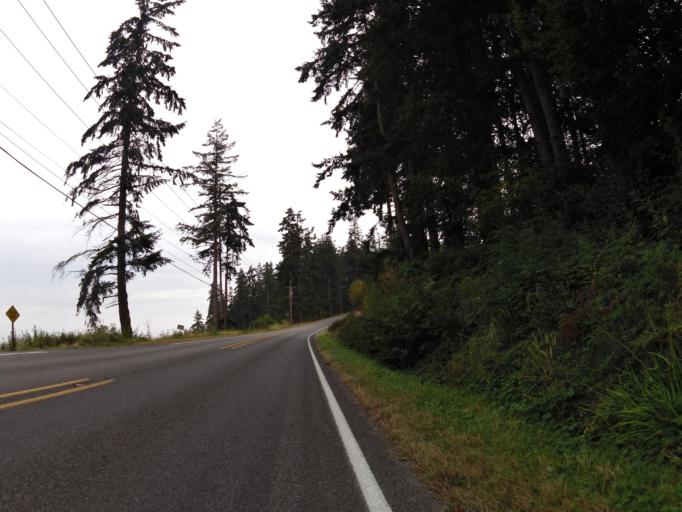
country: US
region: Washington
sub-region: Jefferson County
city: Port Hadlock-Irondale
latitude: 48.0161
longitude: -122.7309
